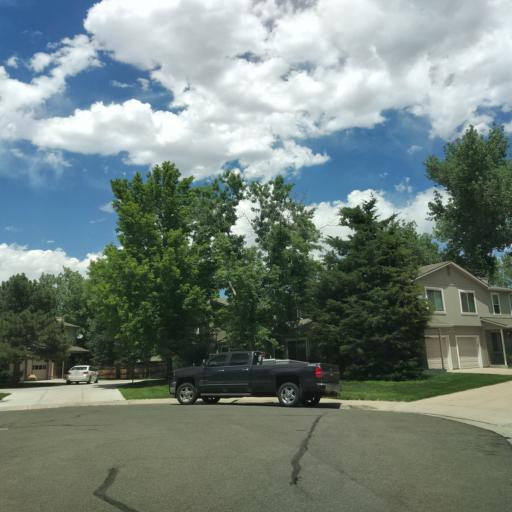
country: US
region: Colorado
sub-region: Jefferson County
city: Lakewood
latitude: 39.6846
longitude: -105.1121
